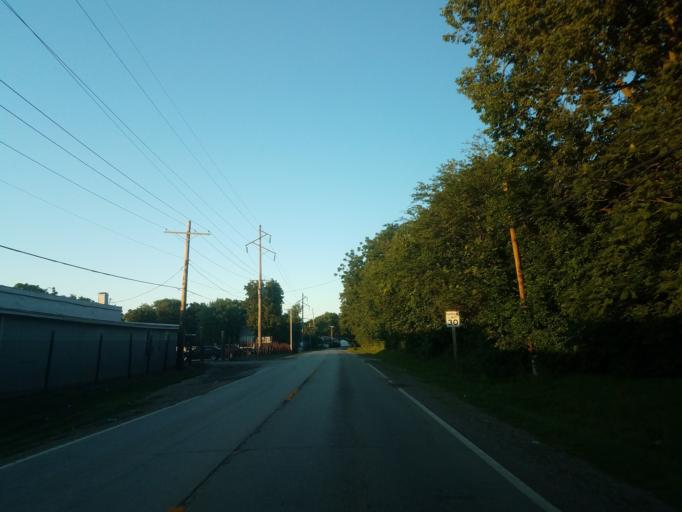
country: US
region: Illinois
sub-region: McLean County
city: Bloomington
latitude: 40.4720
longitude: -89.0208
